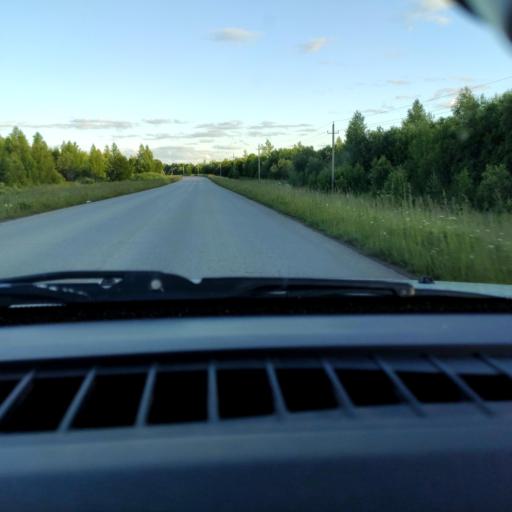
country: RU
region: Perm
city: Polazna
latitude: 58.2029
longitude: 56.5316
